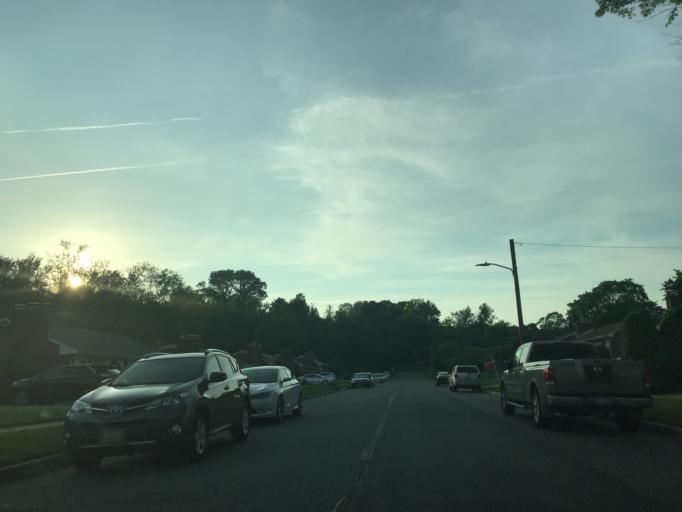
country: US
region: Maryland
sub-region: Harford County
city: North Bel Air
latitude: 39.5324
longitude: -76.3563
